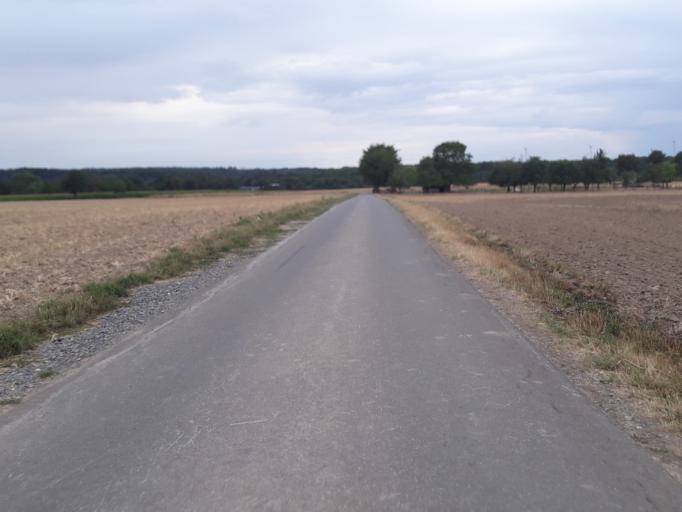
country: DE
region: North Rhine-Westphalia
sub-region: Regierungsbezirk Detmold
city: Paderborn
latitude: 51.6795
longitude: 8.7268
